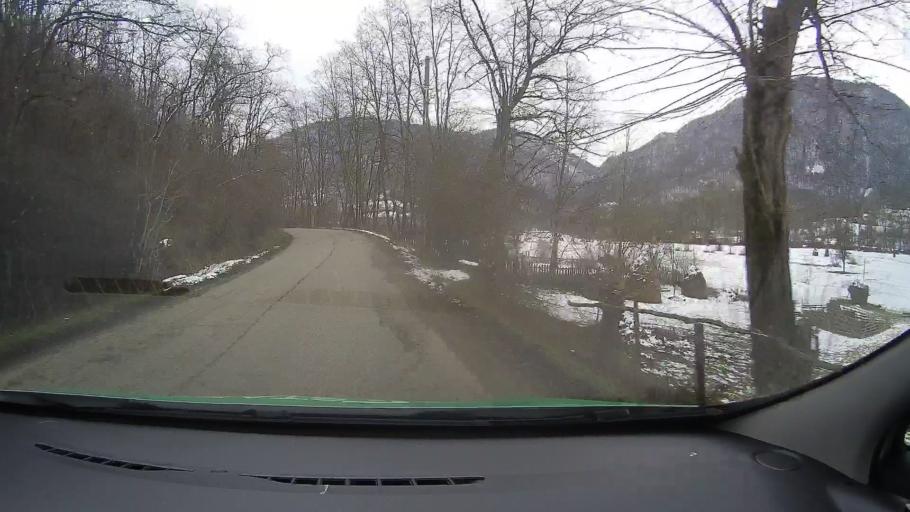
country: RO
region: Hunedoara
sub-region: Comuna Balsa
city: Balsa
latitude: 46.0233
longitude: 23.1179
